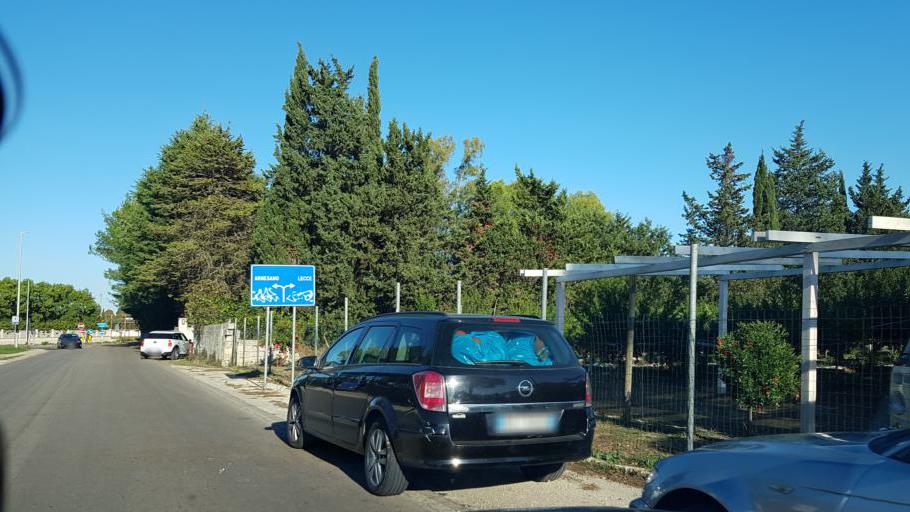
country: IT
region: Apulia
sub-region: Provincia di Lecce
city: Arnesano
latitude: 40.3348
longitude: 18.1012
